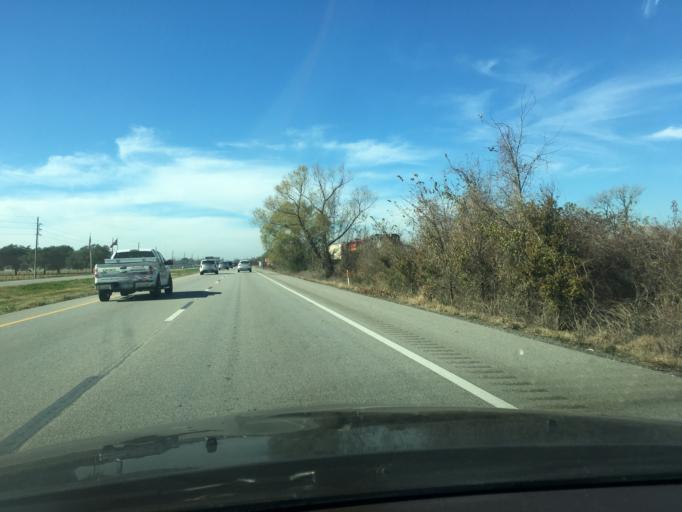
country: US
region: Texas
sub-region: Fort Bend County
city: Pecan Grove
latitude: 29.5984
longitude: -95.7181
